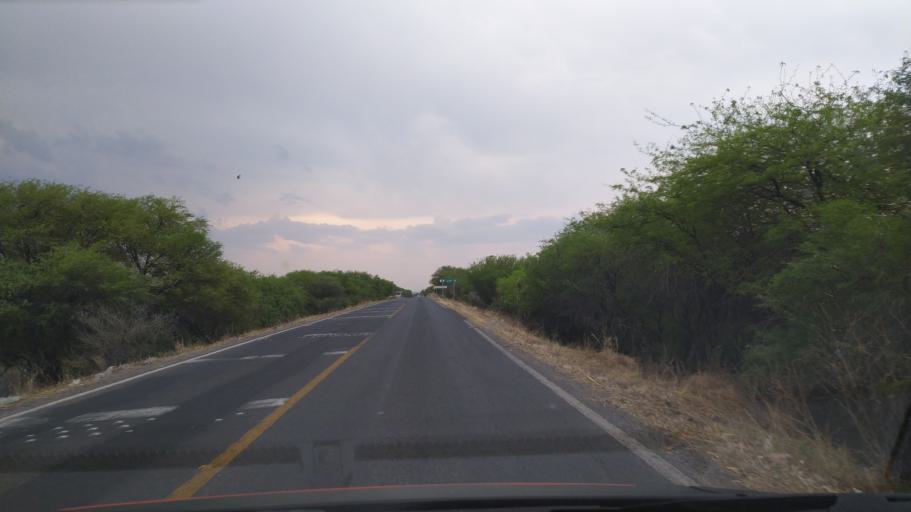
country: MX
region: Guanajuato
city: Ciudad Manuel Doblado
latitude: 20.7518
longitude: -101.9233
